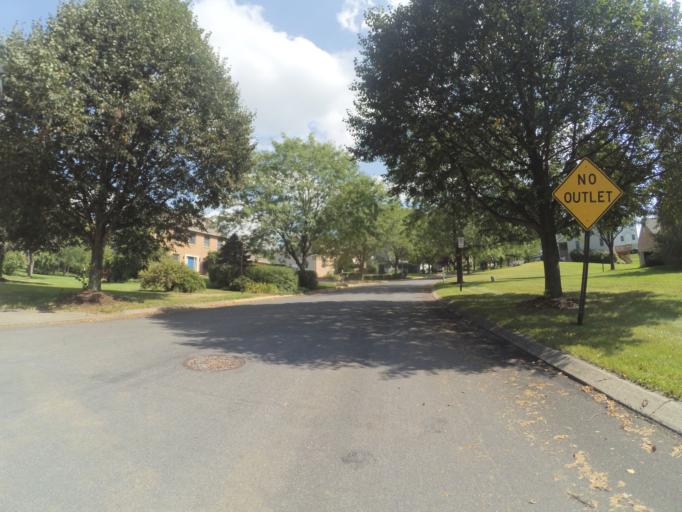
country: US
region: Pennsylvania
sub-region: Centre County
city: Houserville
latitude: 40.8162
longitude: -77.8286
